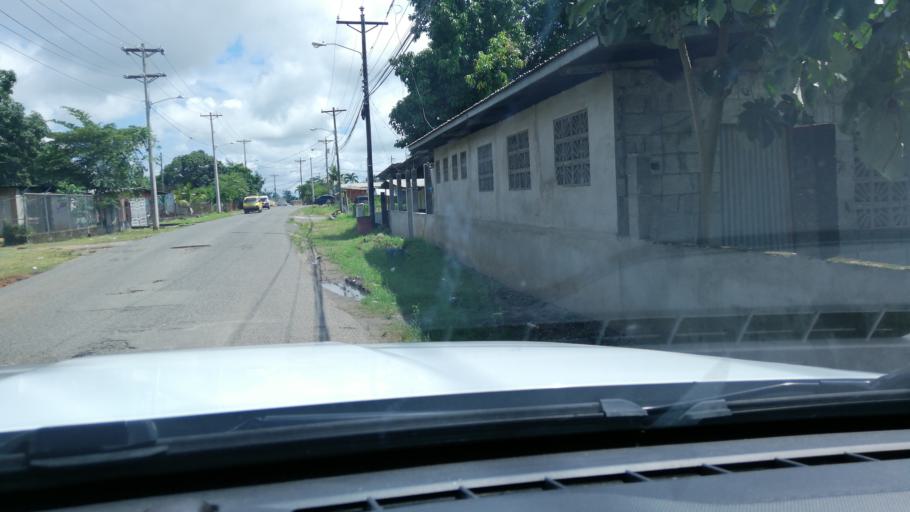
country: PA
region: Panama
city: Cabra Numero Uno
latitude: 9.1116
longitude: -79.3439
